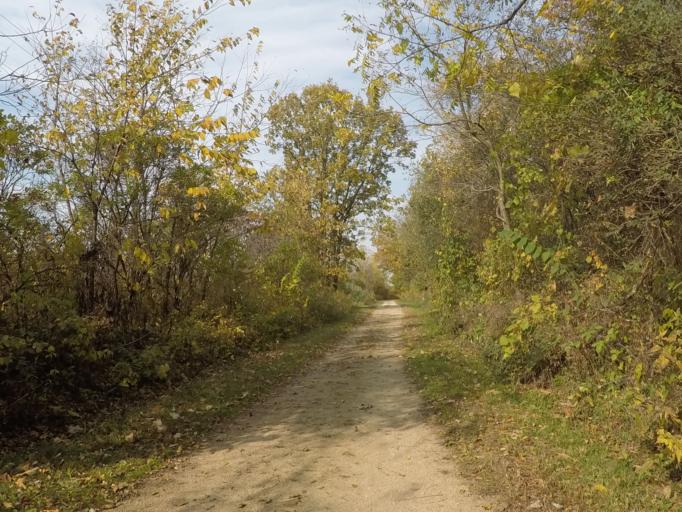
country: US
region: Wisconsin
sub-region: Iowa County
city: Barneveld
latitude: 43.0142
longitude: -89.8227
